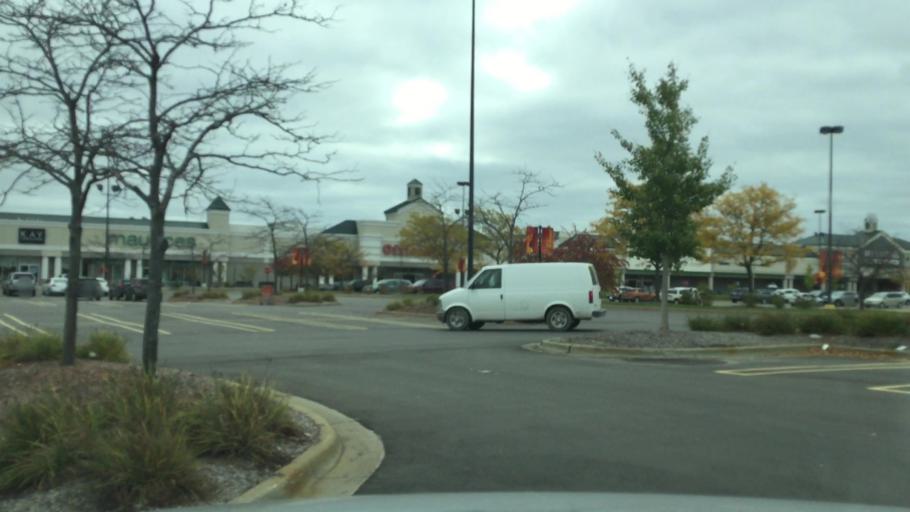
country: US
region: Michigan
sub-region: Oakland County
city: Waterford
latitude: 42.6593
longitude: -83.4664
